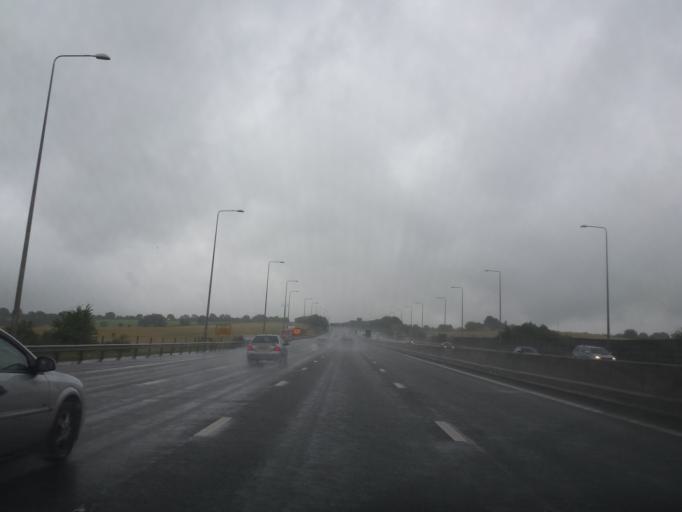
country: GB
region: England
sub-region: Derbyshire
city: Pinxton
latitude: 53.0887
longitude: -1.3038
